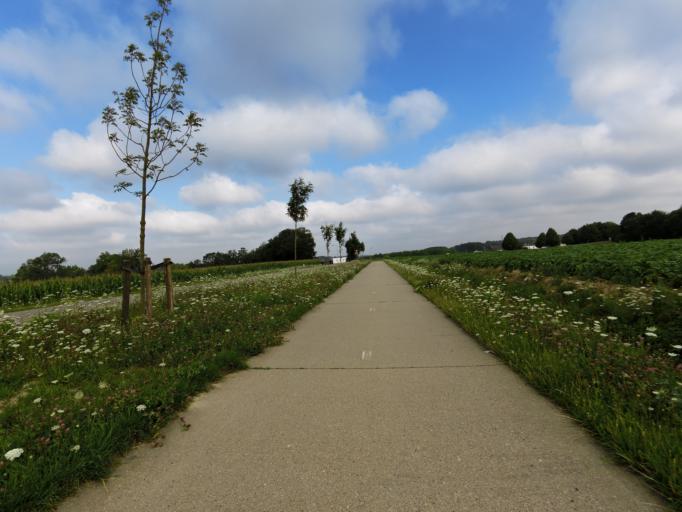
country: NL
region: Limburg
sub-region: Gemeente Heerlen
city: Nieuw-Lotbroek
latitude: 50.9071
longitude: 5.9183
